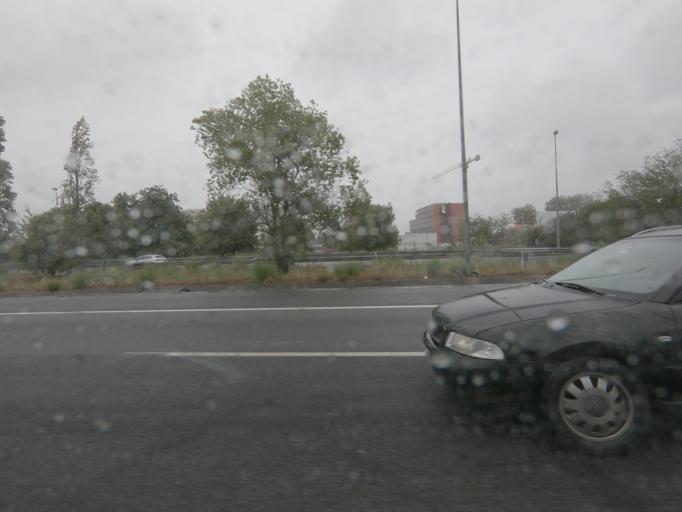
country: PT
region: Porto
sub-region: Porto
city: Porto
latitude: 41.1714
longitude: -8.6021
